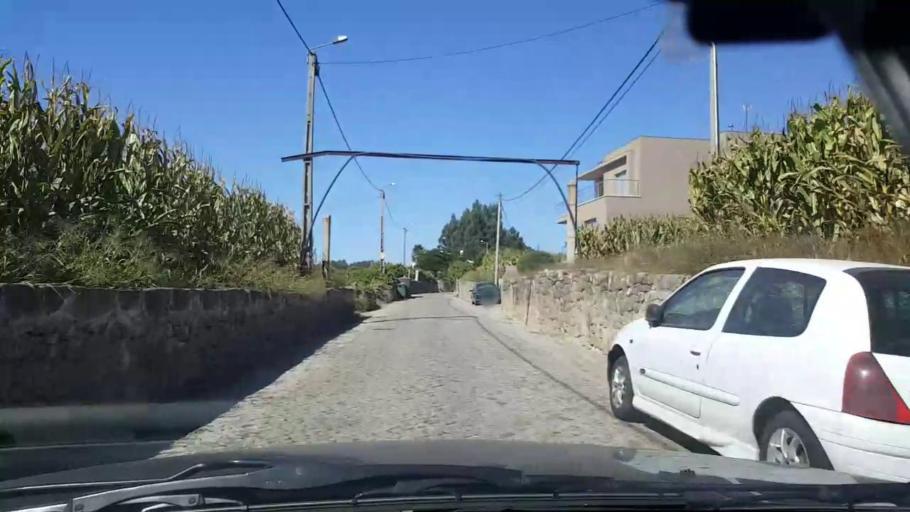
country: PT
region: Porto
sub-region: Vila do Conde
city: Arvore
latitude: 41.3136
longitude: -8.6728
